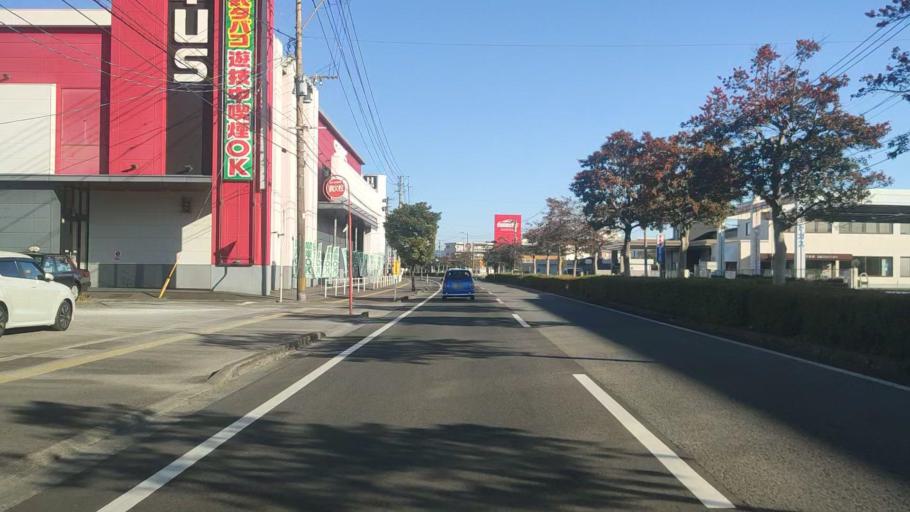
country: JP
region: Miyazaki
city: Nobeoka
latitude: 32.5671
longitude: 131.6830
